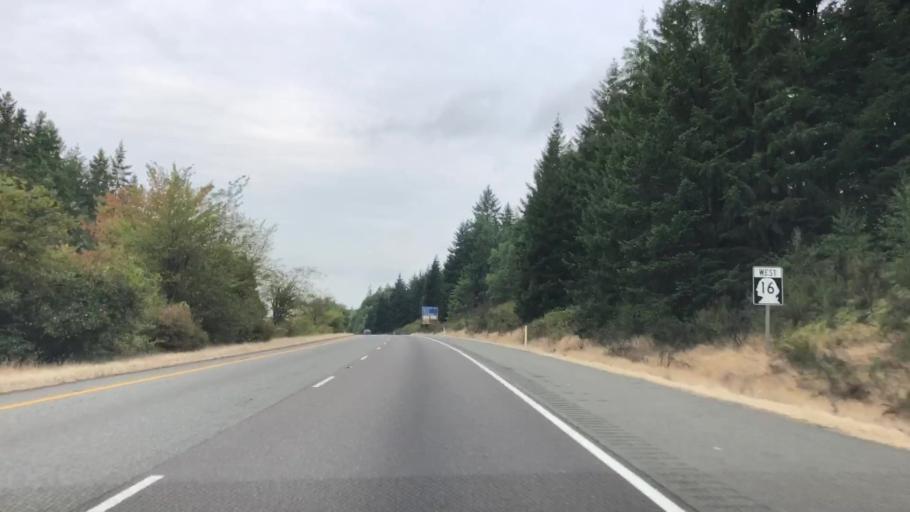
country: US
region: Washington
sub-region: Kitsap County
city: Bethel
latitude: 47.5092
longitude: -122.6504
